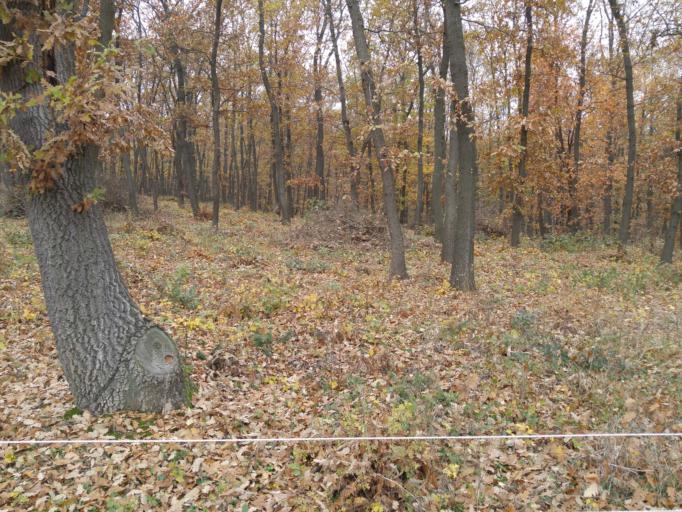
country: HU
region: Pest
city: Biatorbagy
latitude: 47.4489
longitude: 18.8532
